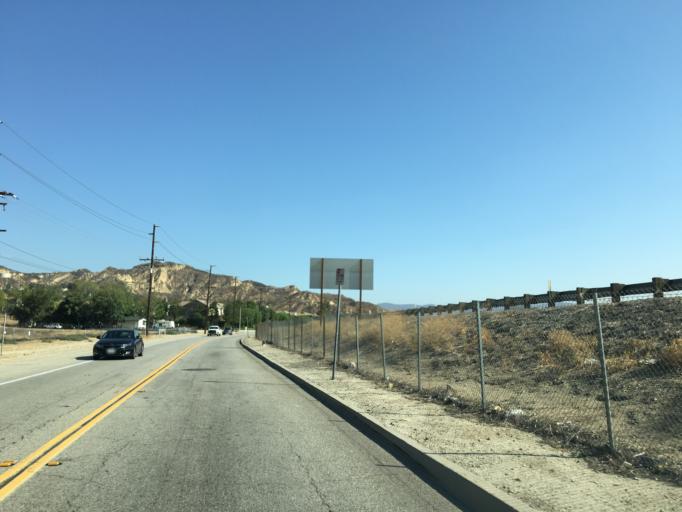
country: US
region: California
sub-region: Los Angeles County
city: Valencia
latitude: 34.4654
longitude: -118.6168
